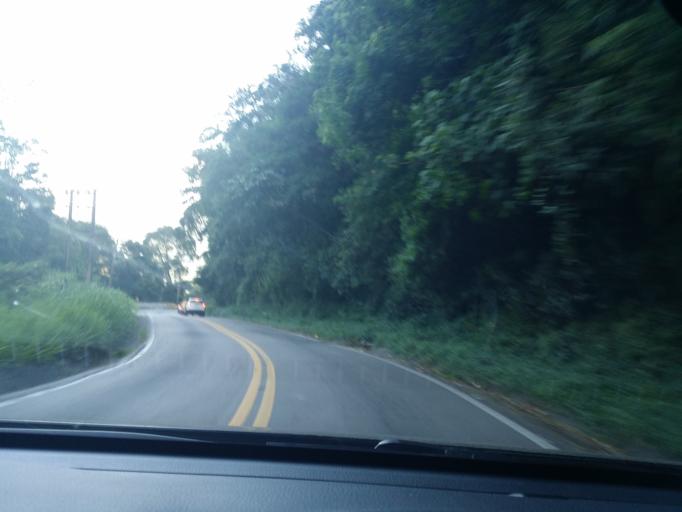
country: BR
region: Sao Paulo
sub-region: Sao Sebastiao
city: Sao Sebastiao
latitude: -23.7854
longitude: -45.5967
